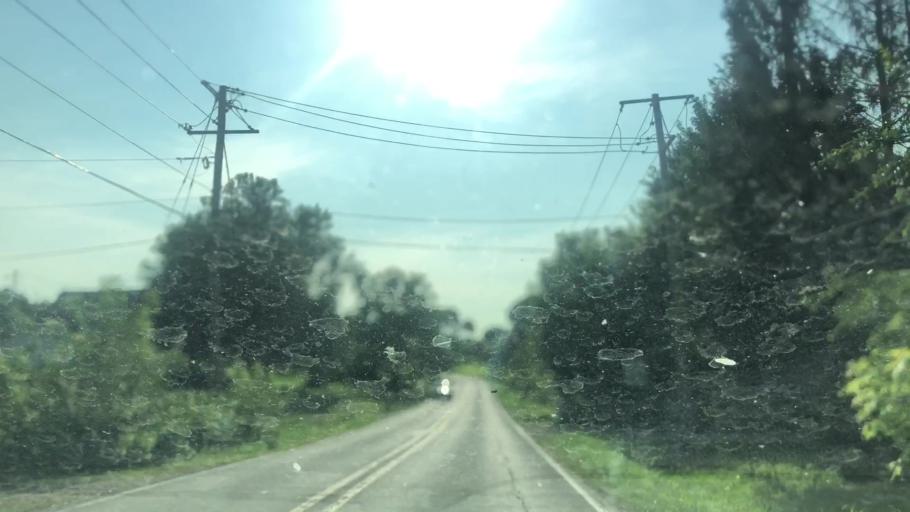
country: US
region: Iowa
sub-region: Marshall County
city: Marshalltown
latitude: 42.0527
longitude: -92.9489
